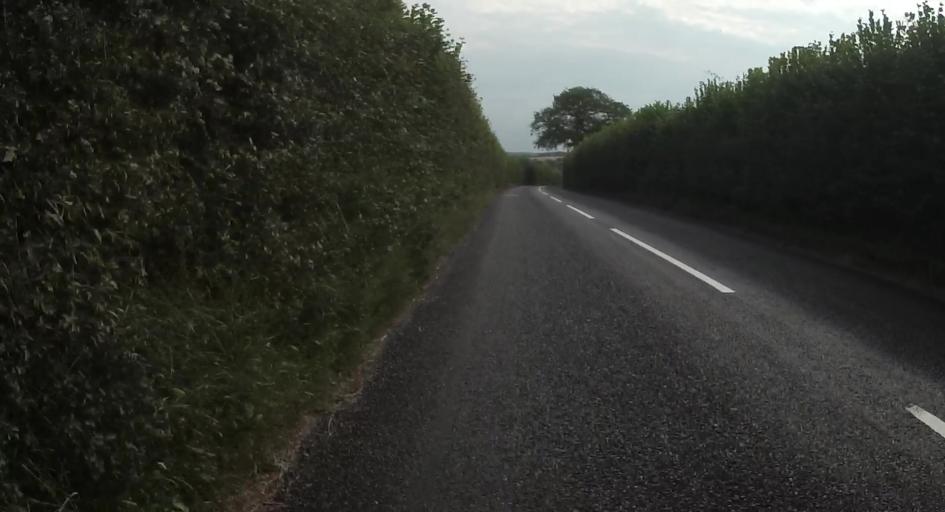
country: GB
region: England
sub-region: Hampshire
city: Swanmore
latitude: 51.0666
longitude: -1.1735
